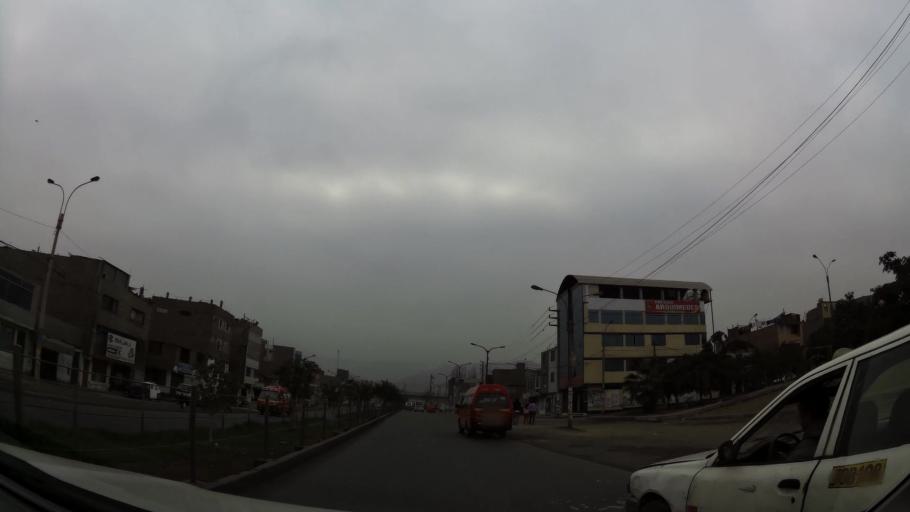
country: PE
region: Lima
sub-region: Lima
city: Independencia
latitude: -11.9602
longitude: -76.9848
